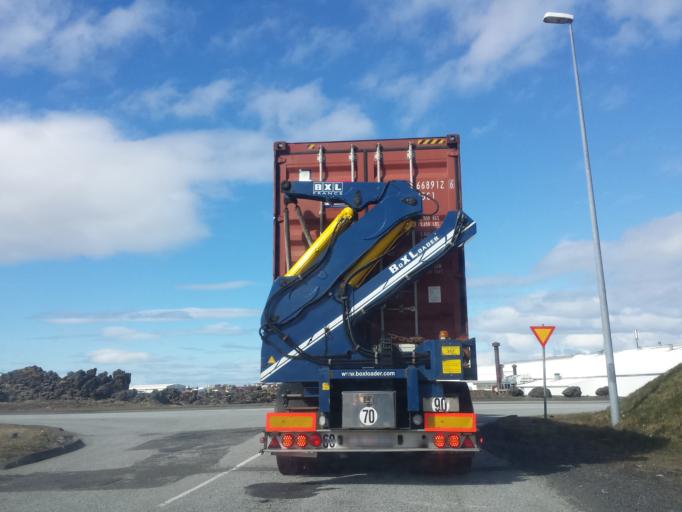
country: IS
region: Capital Region
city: Gardabaer
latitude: 64.0773
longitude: -21.9287
